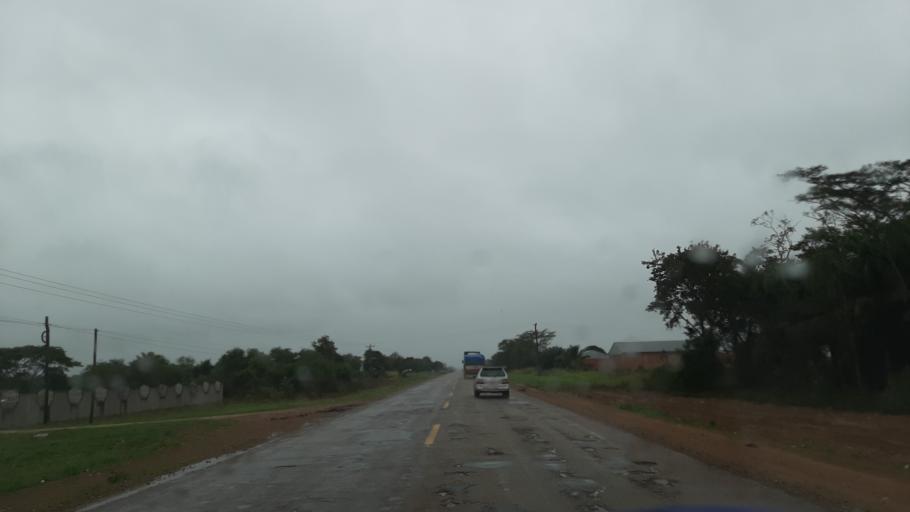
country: BO
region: Santa Cruz
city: Okinawa Numero Uno
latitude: -16.8831
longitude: -62.6141
